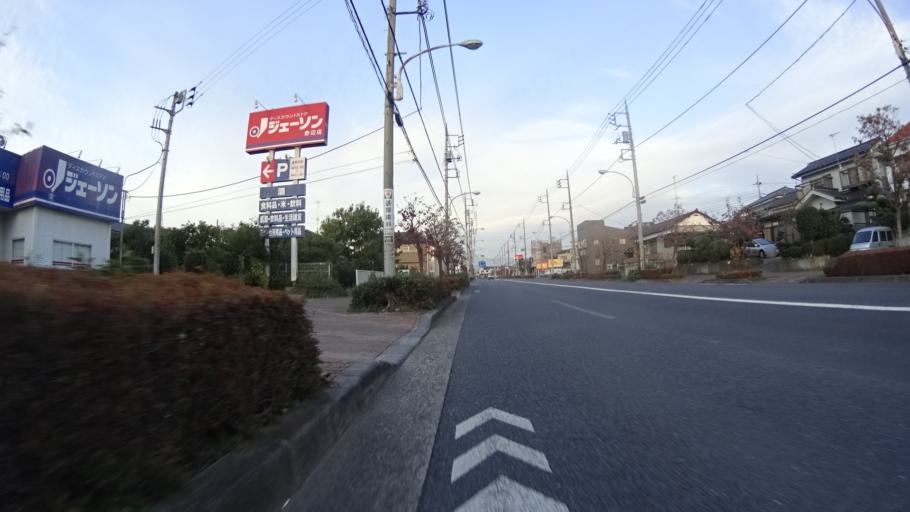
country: JP
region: Tokyo
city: Fussa
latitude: 35.7223
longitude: 139.3068
